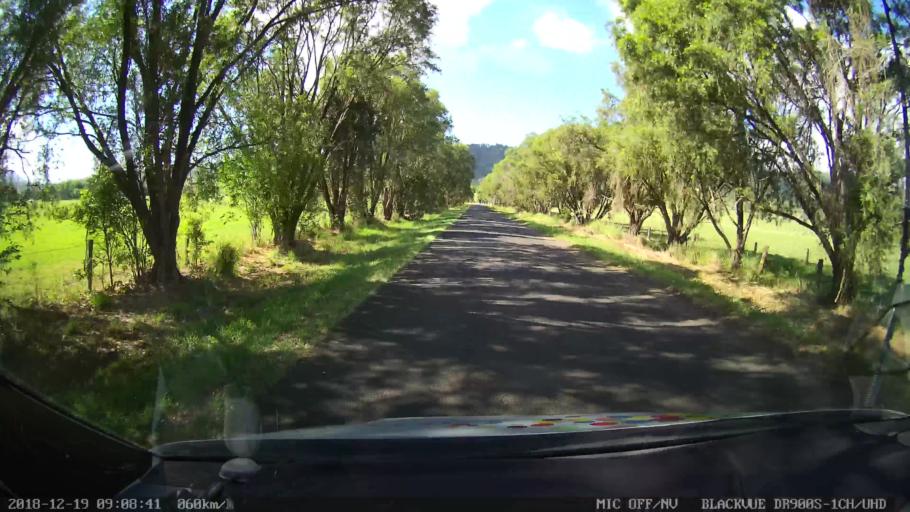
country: AU
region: New South Wales
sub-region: Kyogle
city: Kyogle
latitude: -28.4836
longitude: 152.9308
